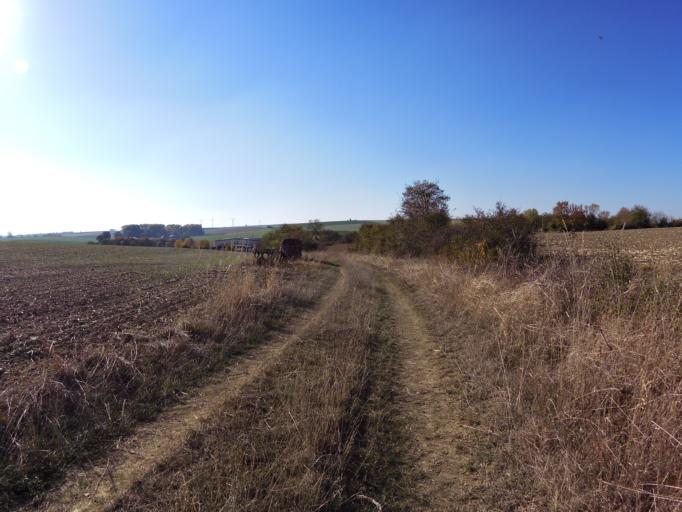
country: DE
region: Bavaria
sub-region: Regierungsbezirk Unterfranken
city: Eibelstadt
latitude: 49.7129
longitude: 9.9700
